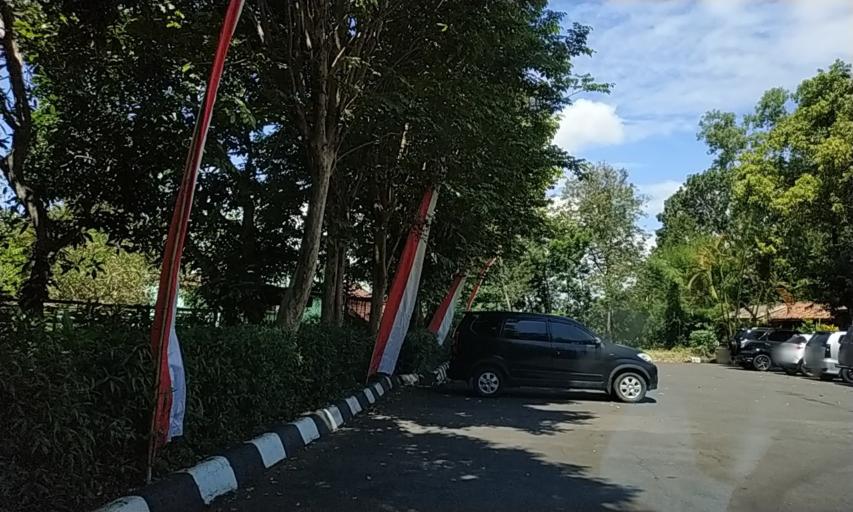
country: ID
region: Central Java
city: Selogiri
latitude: -7.8141
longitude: 110.9503
